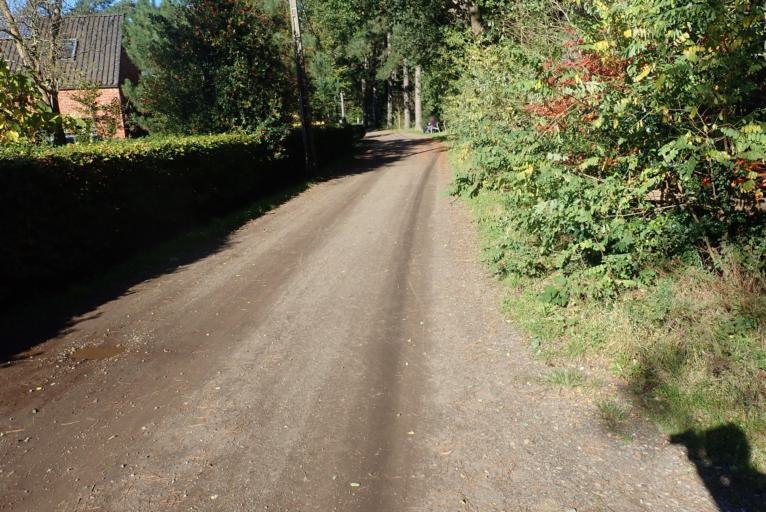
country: BE
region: Flanders
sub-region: Provincie Antwerpen
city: Westerlo
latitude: 51.0921
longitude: 4.8933
